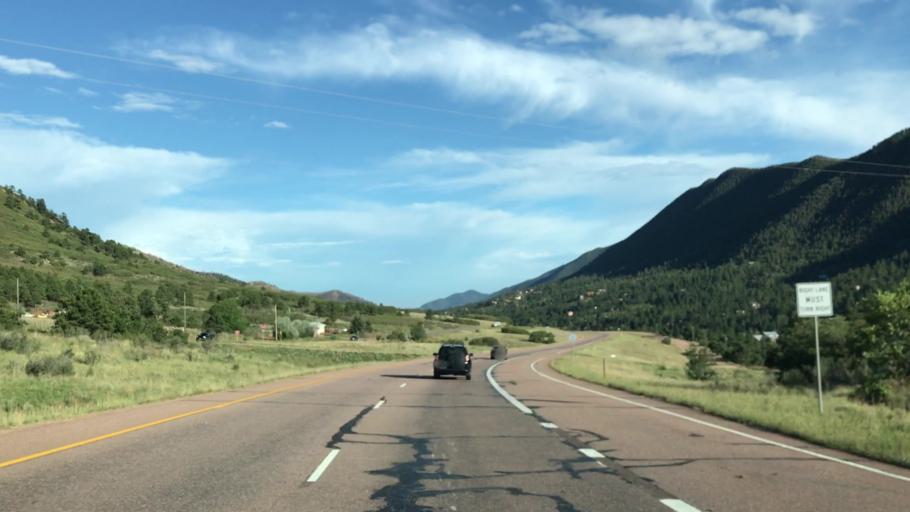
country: US
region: Colorado
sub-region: El Paso County
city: Cascade-Chipita Park
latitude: 38.9309
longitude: -105.0009
